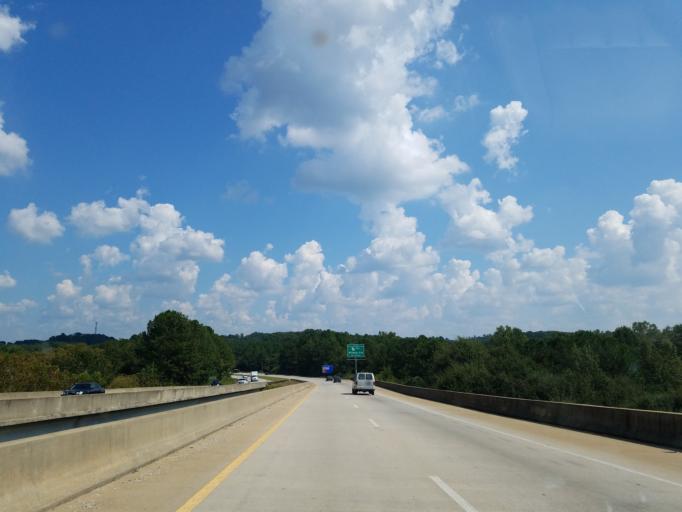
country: US
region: Georgia
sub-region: Clarke County
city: Athens
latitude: 33.9159
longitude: -83.3936
